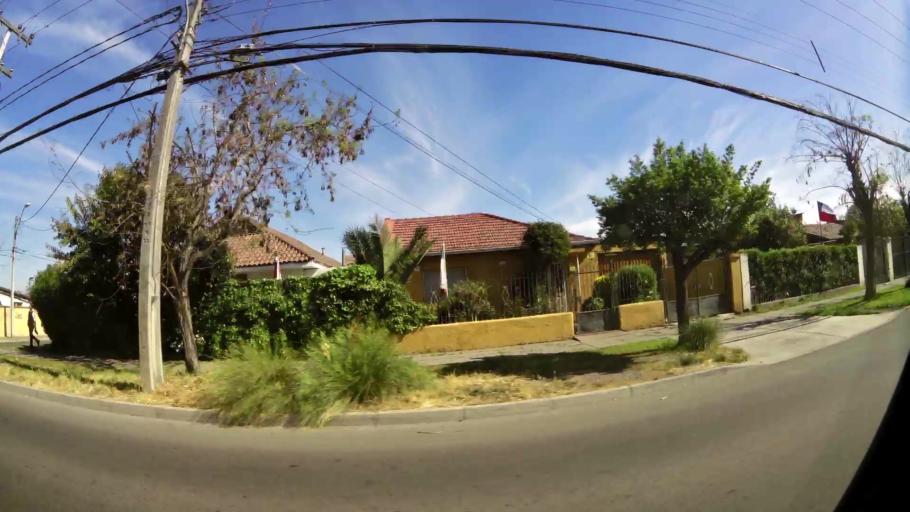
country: CL
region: Santiago Metropolitan
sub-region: Provincia de Santiago
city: Lo Prado
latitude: -33.4920
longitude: -70.7073
